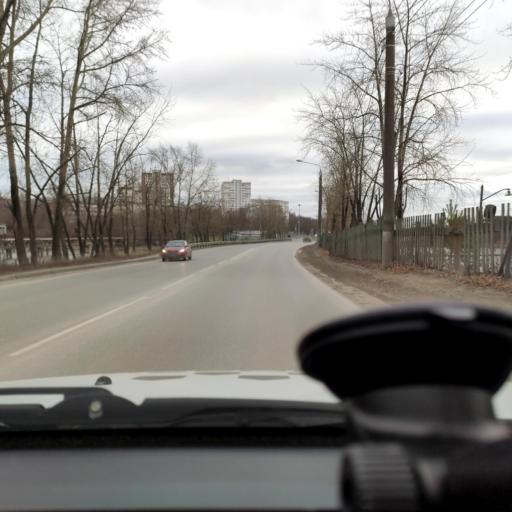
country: RU
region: Perm
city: Perm
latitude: 58.1172
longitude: 56.3682
